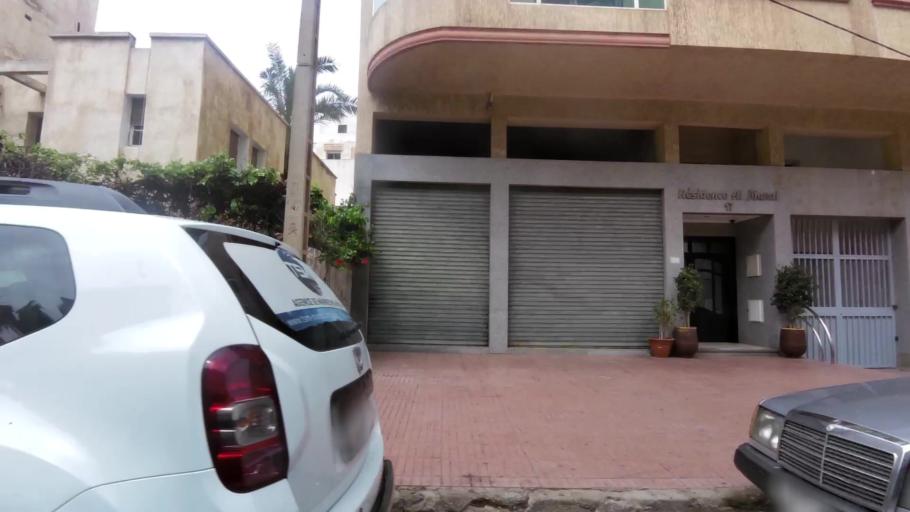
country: MA
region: Grand Casablanca
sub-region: Casablanca
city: Casablanca
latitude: 33.5994
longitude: -7.6473
